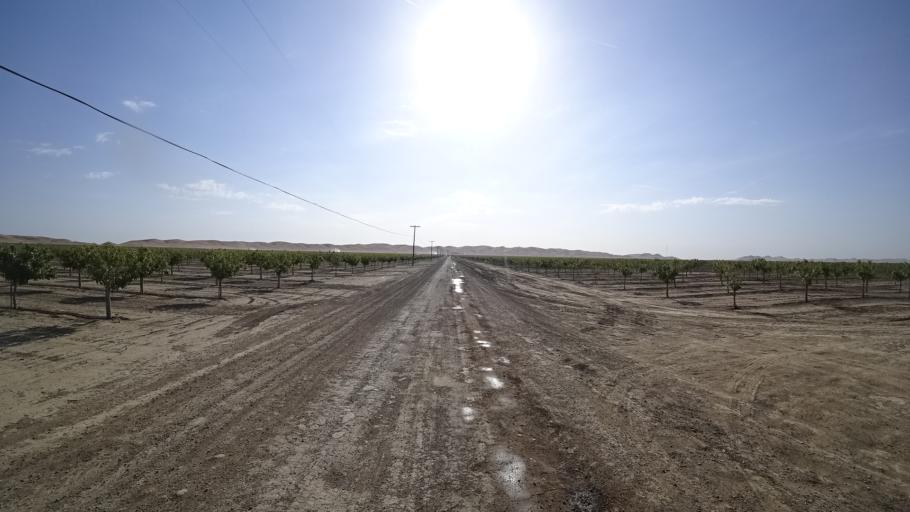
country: US
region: California
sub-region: Kings County
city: Avenal
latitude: 35.8179
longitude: -120.0650
